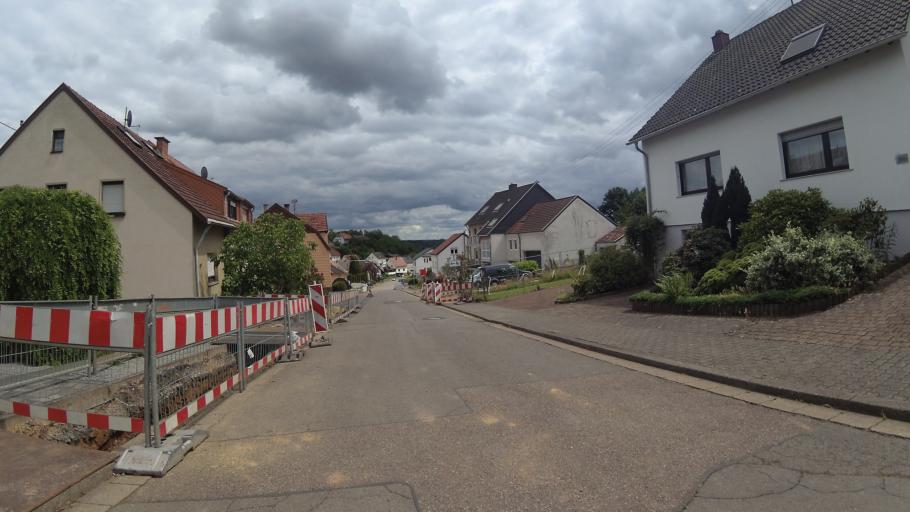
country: DE
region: Saarland
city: Nalbach
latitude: 49.3823
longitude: 6.7774
